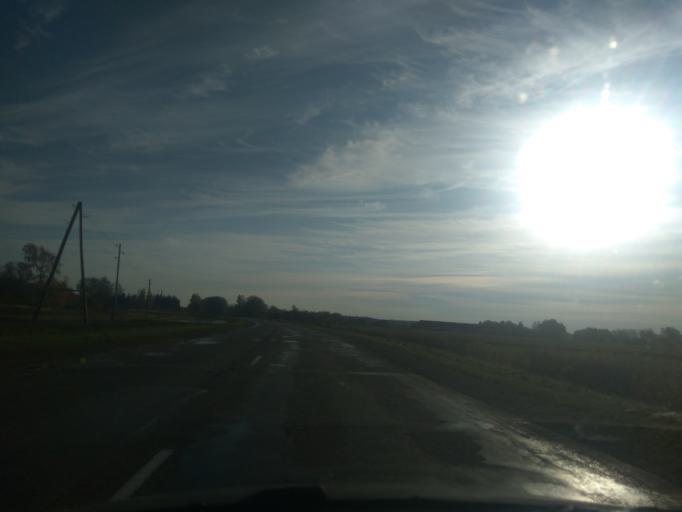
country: LV
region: Ventspils
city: Ventspils
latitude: 57.3123
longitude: 21.5562
